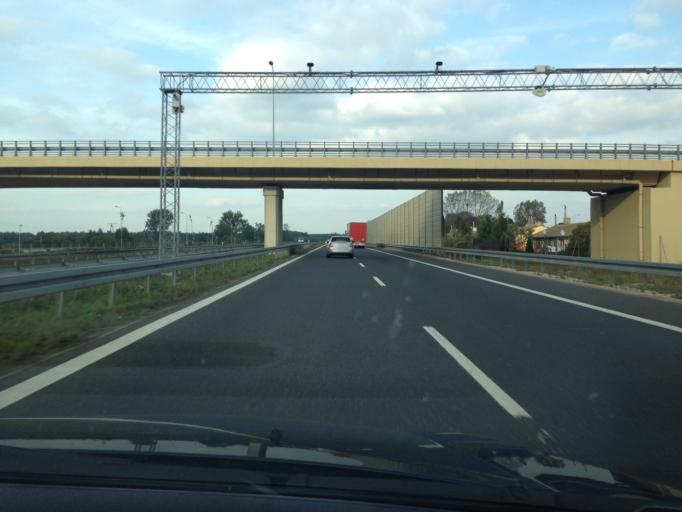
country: PL
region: Greater Poland Voivodeship
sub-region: Powiat gnieznienski
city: Lubowo
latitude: 52.4726
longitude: 17.4089
